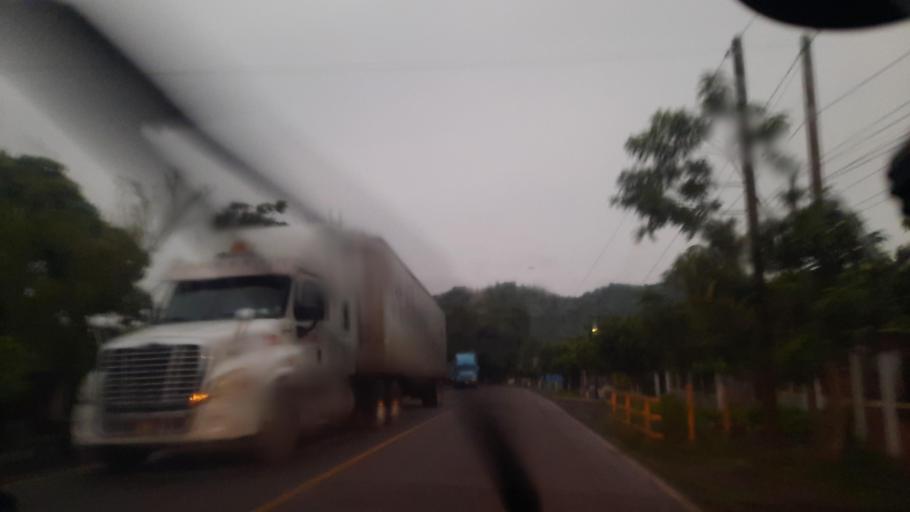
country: GT
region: Jutiapa
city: Atescatempa
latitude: 14.2107
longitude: -89.6816
